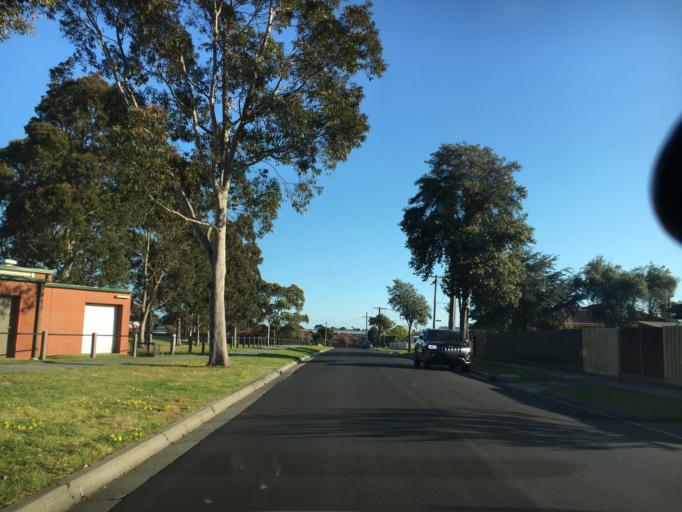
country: AU
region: Victoria
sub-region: Kingston
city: Clayton South
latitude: -37.9351
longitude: 145.1223
